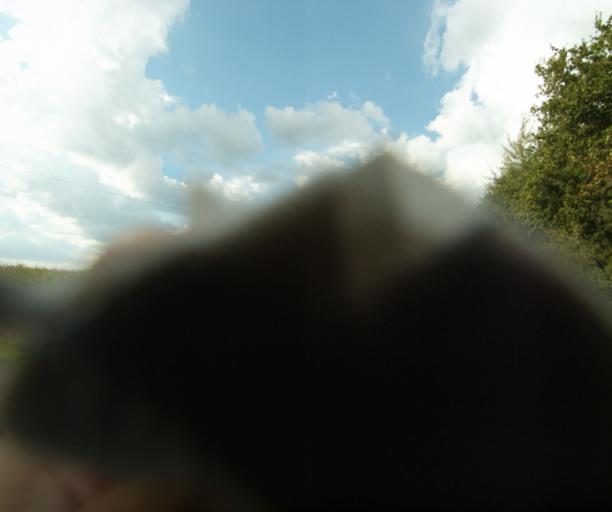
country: FR
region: Midi-Pyrenees
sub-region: Departement du Gers
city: Cazaubon
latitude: 43.8919
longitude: -0.0826
